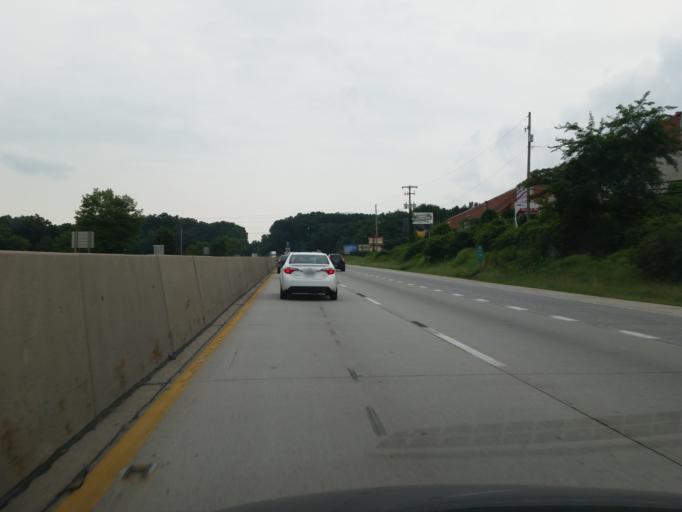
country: US
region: Pennsylvania
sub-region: York County
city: Valley Green
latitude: 40.1802
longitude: -76.8378
